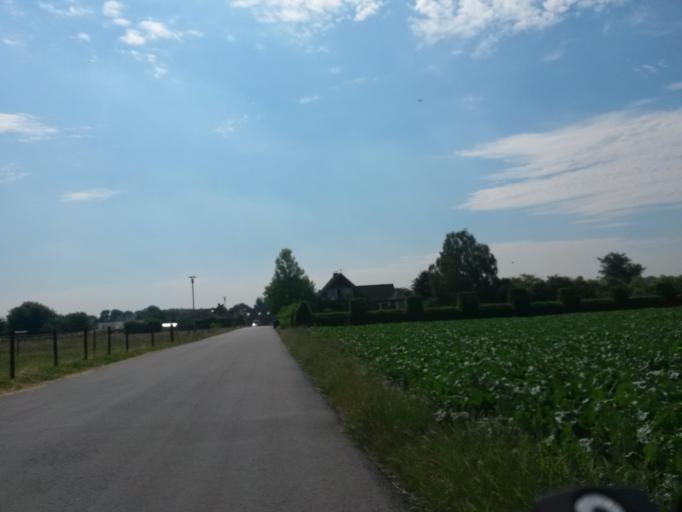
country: DE
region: North Rhine-Westphalia
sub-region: Regierungsbezirk Dusseldorf
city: Rheurdt
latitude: 51.4341
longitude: 6.4254
